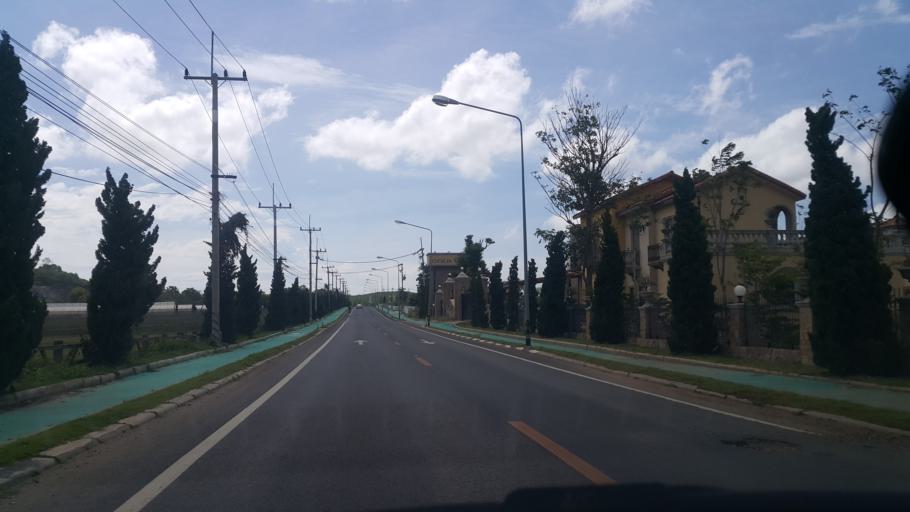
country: TH
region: Rayong
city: Ban Chang
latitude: 12.7628
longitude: 100.9623
